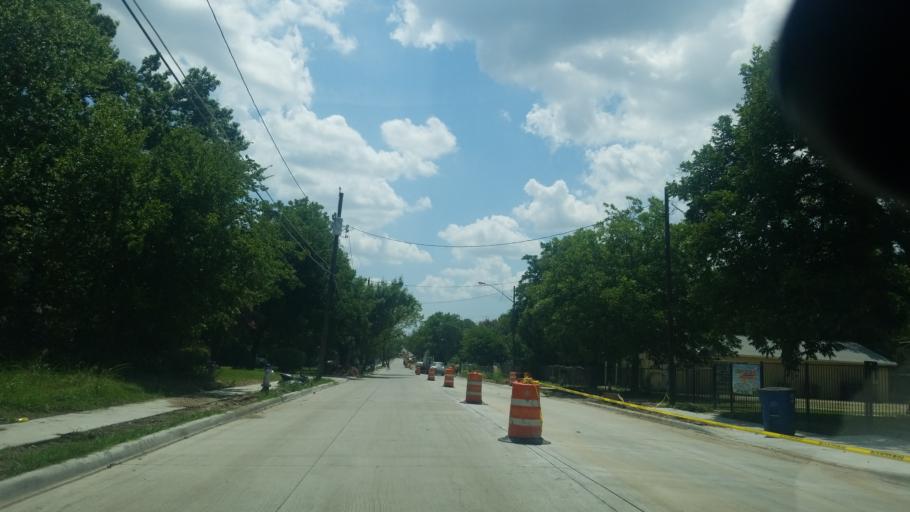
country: US
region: Texas
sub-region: Dallas County
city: Dallas
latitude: 32.7133
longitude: -96.7684
